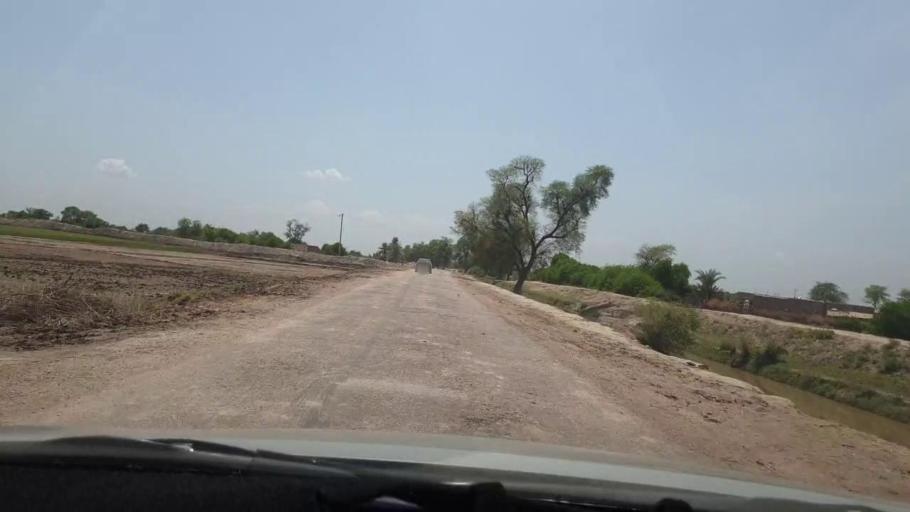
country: PK
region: Sindh
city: Pano Aqil
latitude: 27.7351
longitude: 69.1904
